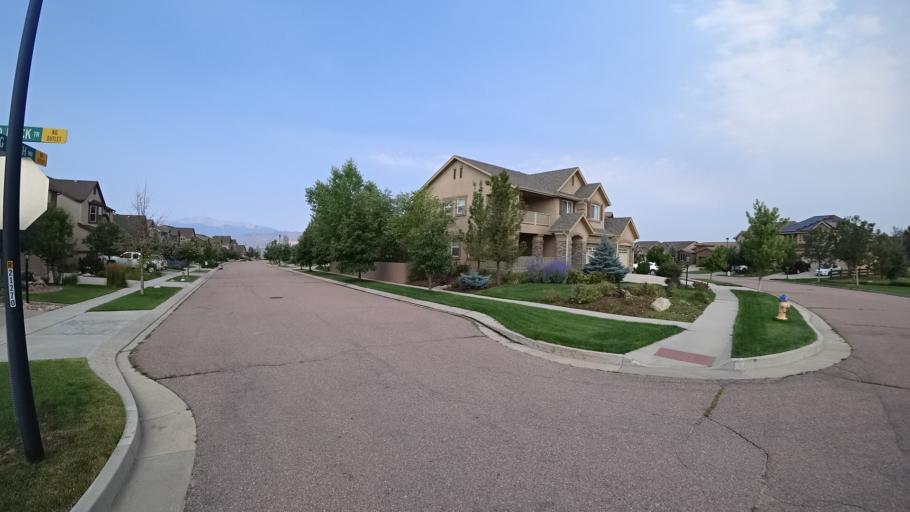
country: US
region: Colorado
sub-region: El Paso County
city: Black Forest
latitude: 38.9699
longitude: -104.7358
